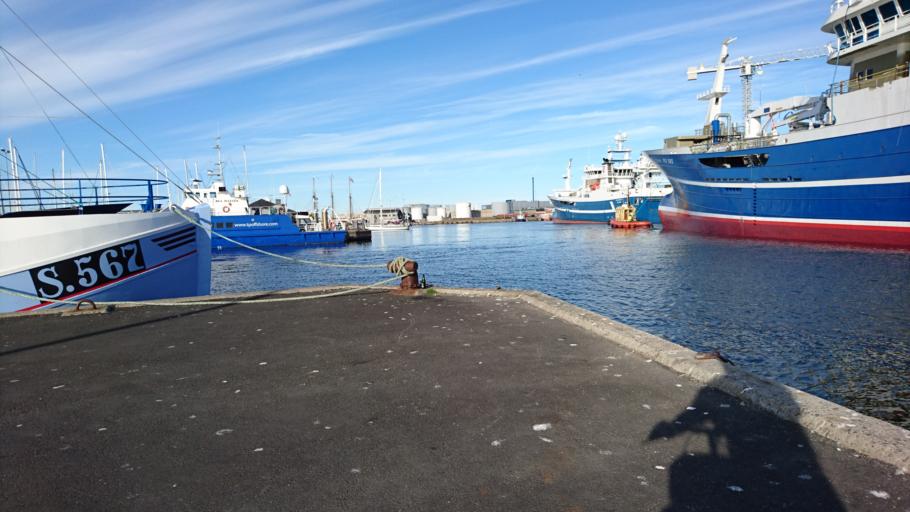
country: DK
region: North Denmark
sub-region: Frederikshavn Kommune
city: Skagen
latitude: 57.7174
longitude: 10.5872
